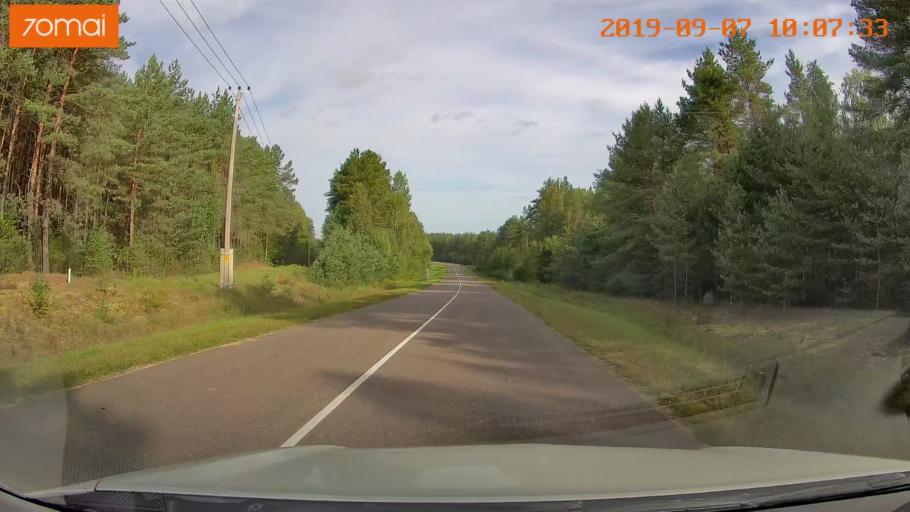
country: BY
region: Grodnenskaya
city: Voranava
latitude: 54.0769
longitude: 25.3961
